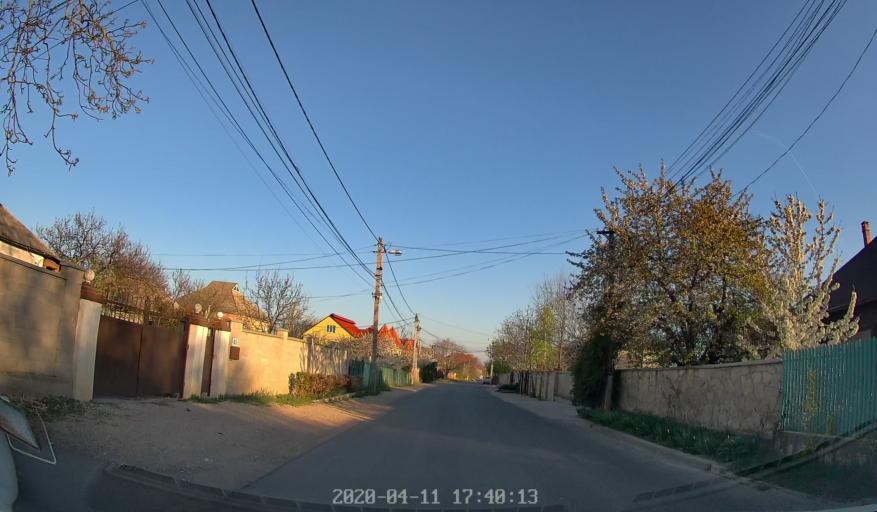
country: MD
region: Laloveni
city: Ialoveni
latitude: 46.9803
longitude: 28.8099
